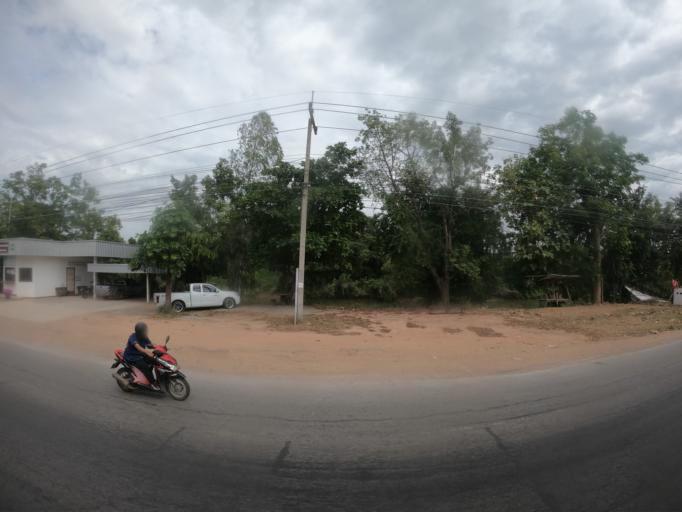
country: TH
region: Maha Sarakham
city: Maha Sarakham
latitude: 16.2192
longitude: 103.2754
